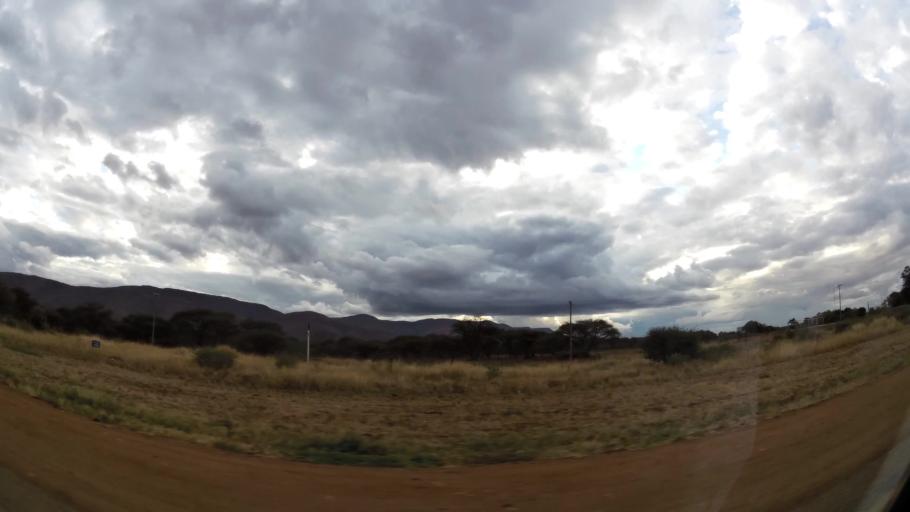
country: ZA
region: Limpopo
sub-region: Waterberg District Municipality
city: Mokopane
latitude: -24.2218
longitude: 29.0035
